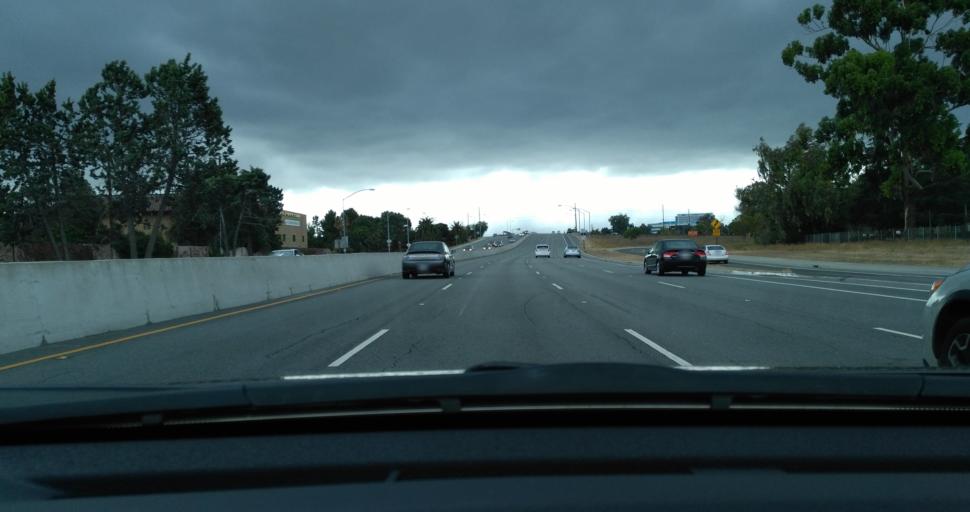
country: US
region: California
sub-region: Santa Clara County
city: Santa Clara
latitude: 37.3916
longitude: -121.9503
